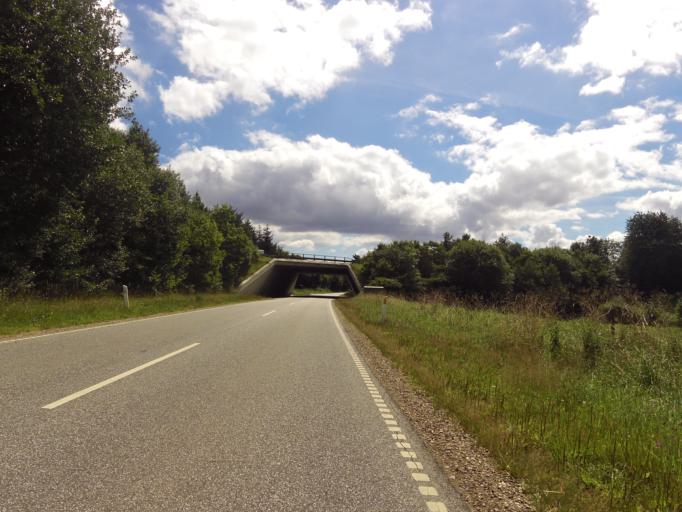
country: DK
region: South Denmark
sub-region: Haderslev Kommune
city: Haderslev
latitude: 55.2742
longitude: 9.4237
